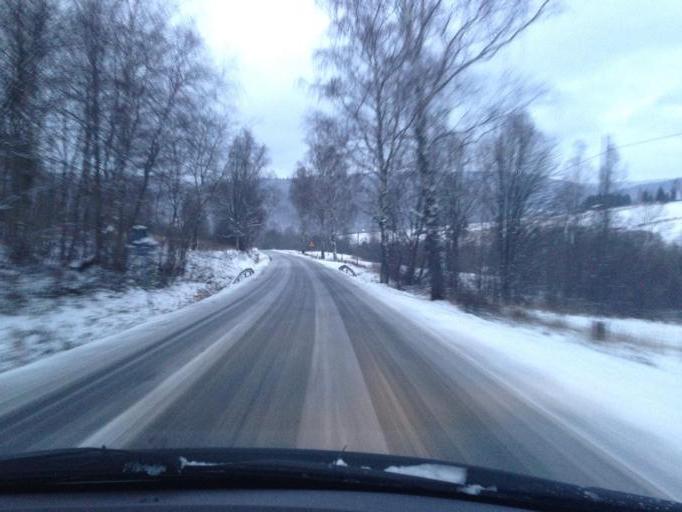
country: PL
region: Subcarpathian Voivodeship
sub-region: Powiat jasielski
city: Krempna
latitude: 49.5226
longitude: 21.5020
